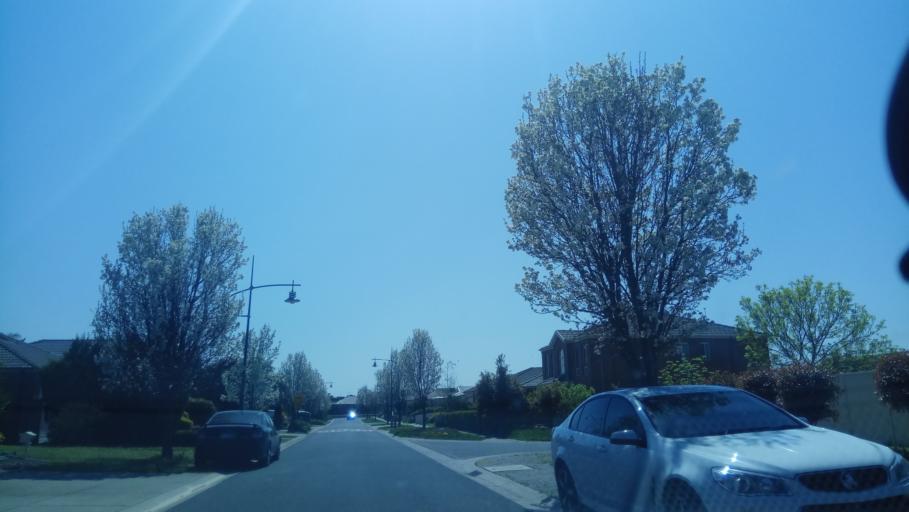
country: AU
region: Victoria
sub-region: Wyndham
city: Point Cook
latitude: -37.8925
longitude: 144.7382
